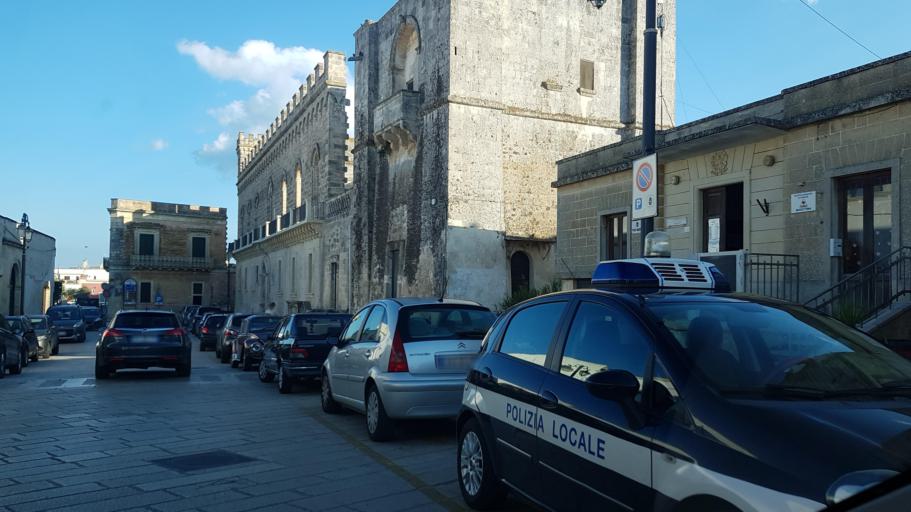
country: IT
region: Apulia
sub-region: Provincia di Lecce
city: Marittima
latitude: 39.9948
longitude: 18.3985
